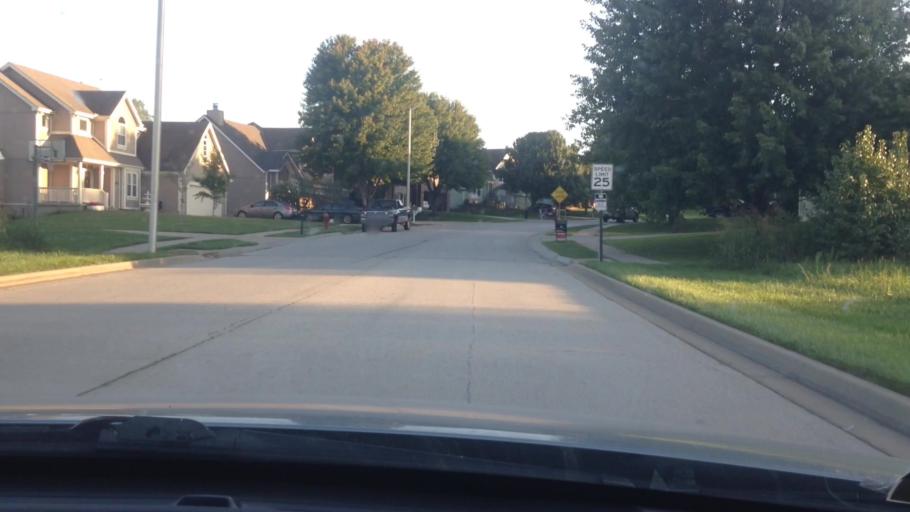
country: US
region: Missouri
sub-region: Clay County
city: Smithville
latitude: 39.3024
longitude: -94.5902
